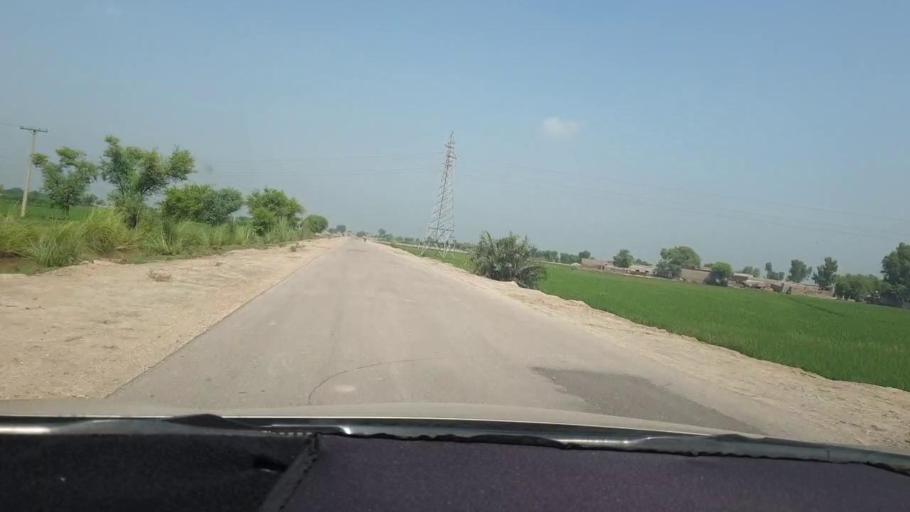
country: PK
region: Sindh
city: Miro Khan
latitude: 27.7784
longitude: 68.0555
